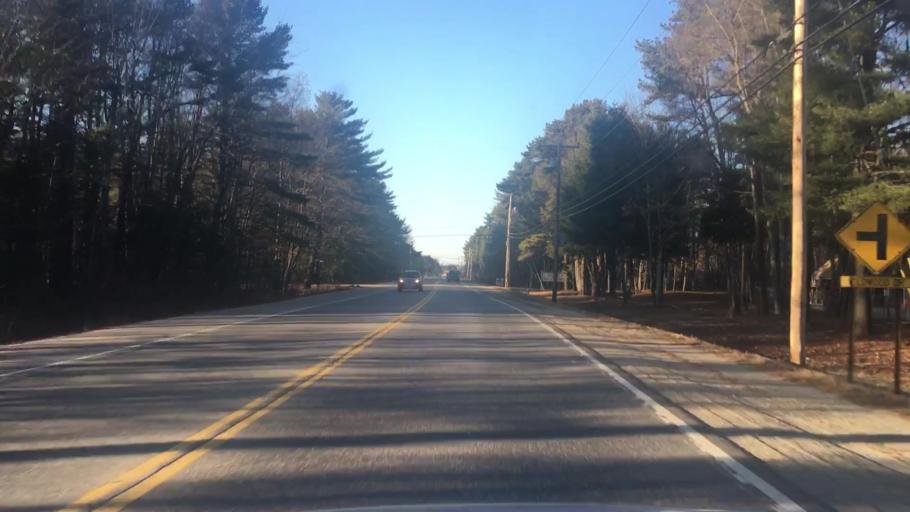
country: US
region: Maine
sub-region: Cumberland County
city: Brunswick
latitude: 43.8979
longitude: -69.9081
